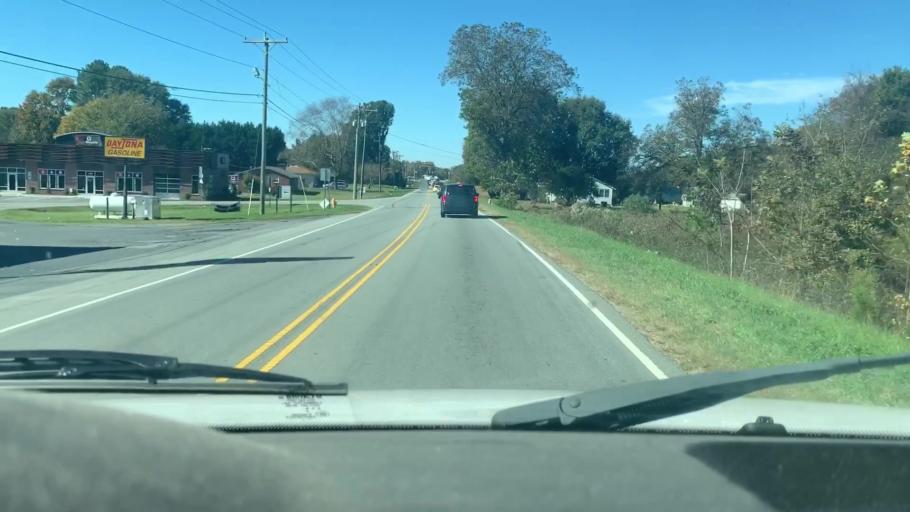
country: US
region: North Carolina
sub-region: Lincoln County
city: Lowesville
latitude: 35.4420
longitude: -80.9837
